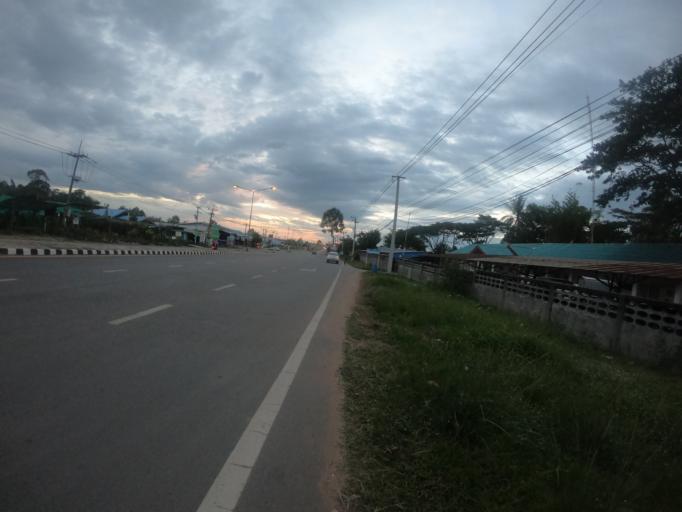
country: TH
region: Surin
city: Kap Choeng
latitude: 14.4520
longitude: 103.6963
